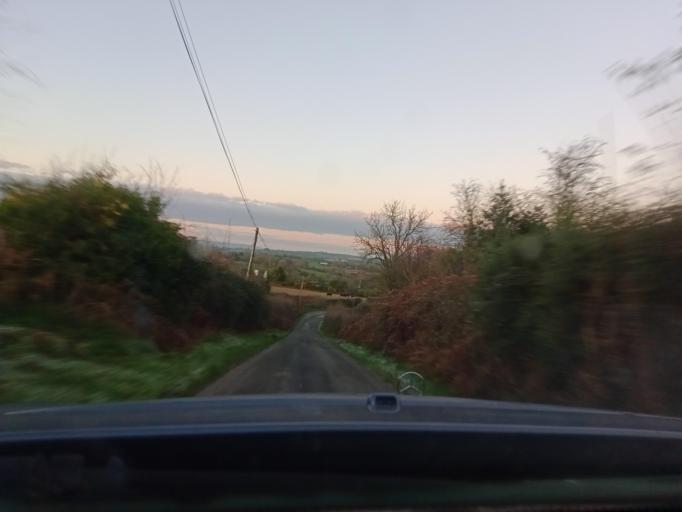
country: IE
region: Leinster
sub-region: Kilkenny
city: Graiguenamanagh
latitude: 52.5852
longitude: -6.9636
